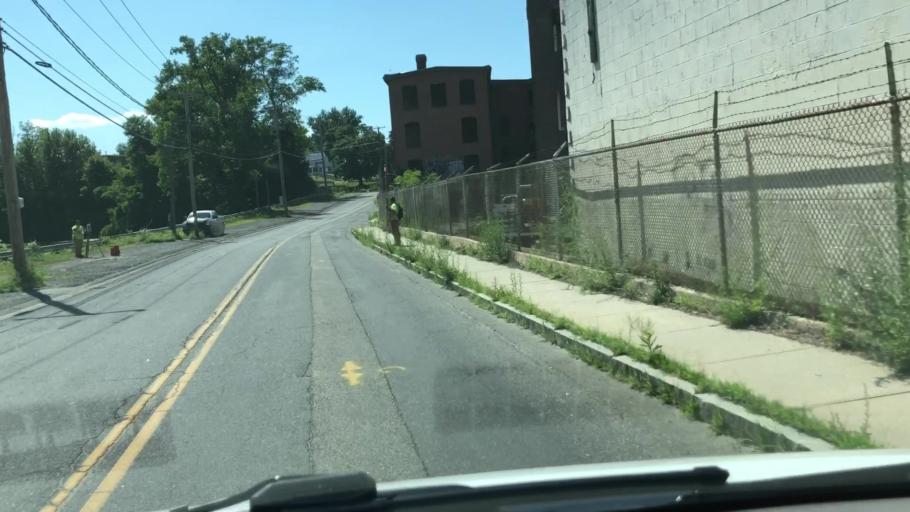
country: US
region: Massachusetts
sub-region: Hampshire County
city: Easthampton
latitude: 42.2758
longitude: -72.6552
